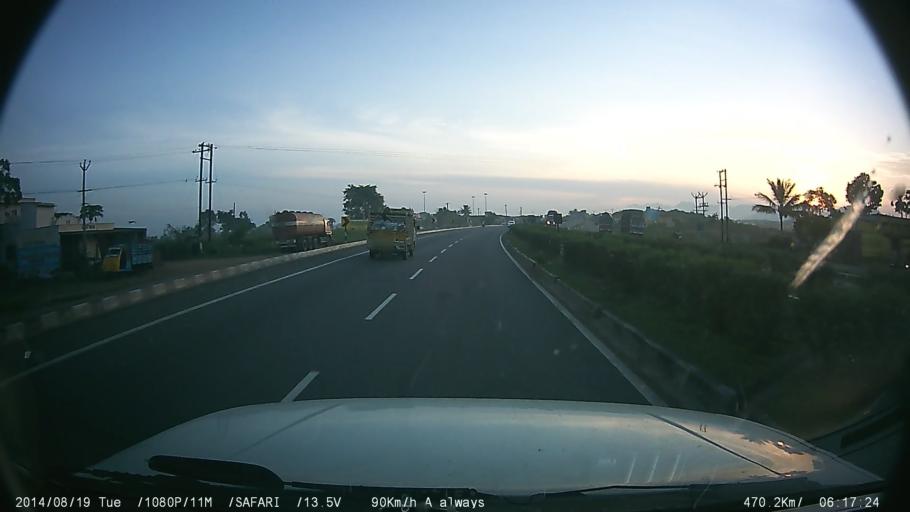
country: IN
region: Tamil Nadu
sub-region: Dharmapuri
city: Dharmapuri
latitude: 11.9950
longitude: 78.0695
